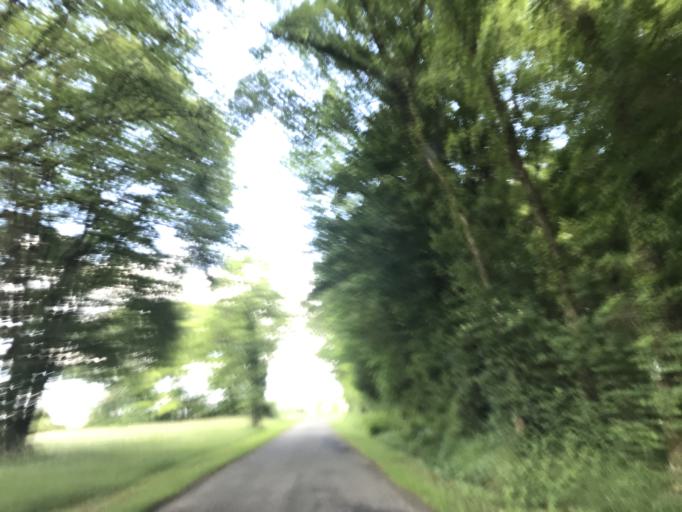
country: FR
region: Aquitaine
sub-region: Departement de la Dordogne
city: Saint-Aulaye
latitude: 45.2628
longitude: 0.1264
